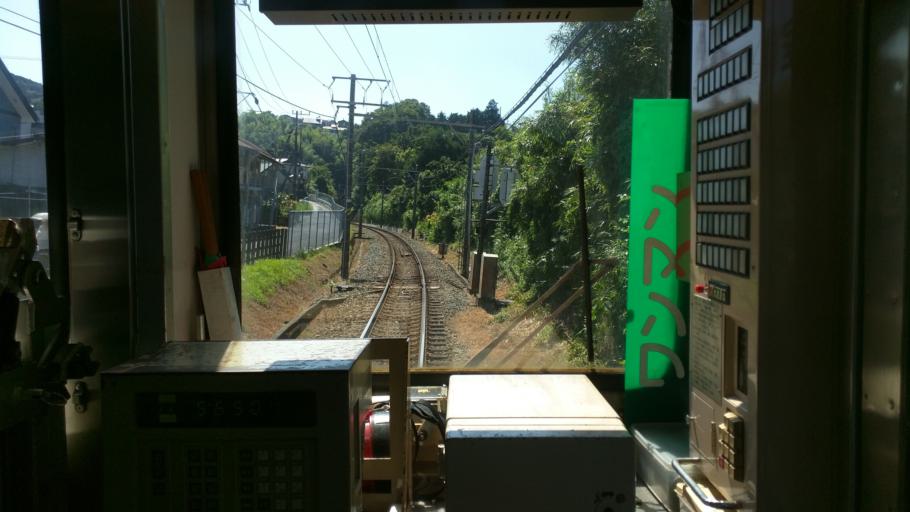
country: JP
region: Shizuoka
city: Ito
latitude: 34.9510
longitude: 139.1232
